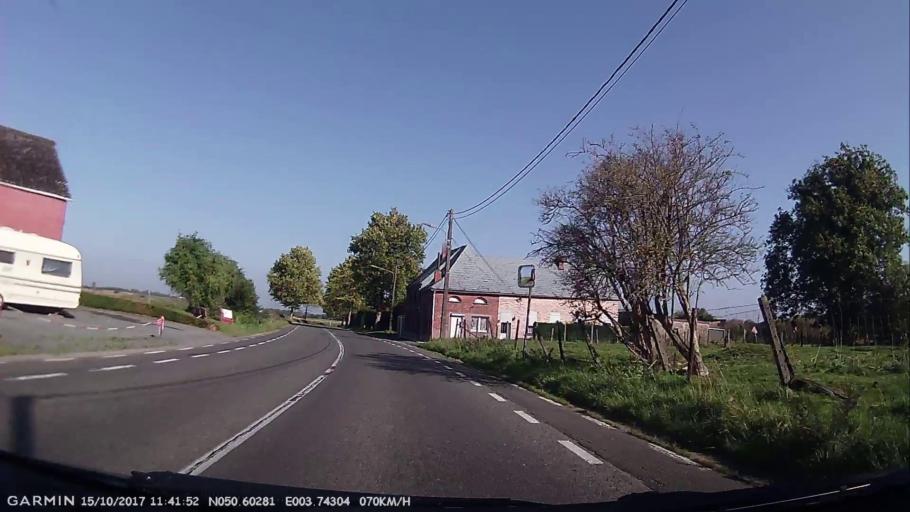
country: BE
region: Wallonia
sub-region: Province du Hainaut
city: Ath
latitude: 50.6029
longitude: 3.7431
